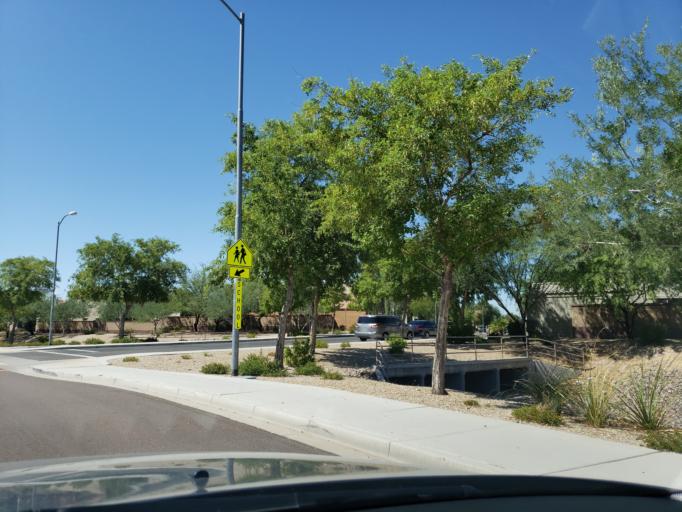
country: US
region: Arizona
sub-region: Maricopa County
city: Sun City West
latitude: 33.6797
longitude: -112.2701
